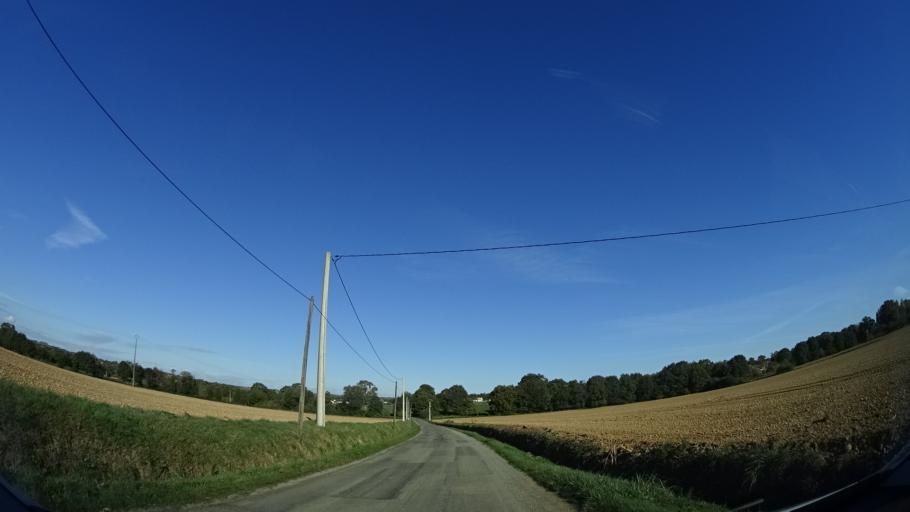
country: FR
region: Brittany
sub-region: Departement d'Ille-et-Vilaine
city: Geveze
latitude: 48.2097
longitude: -1.7743
